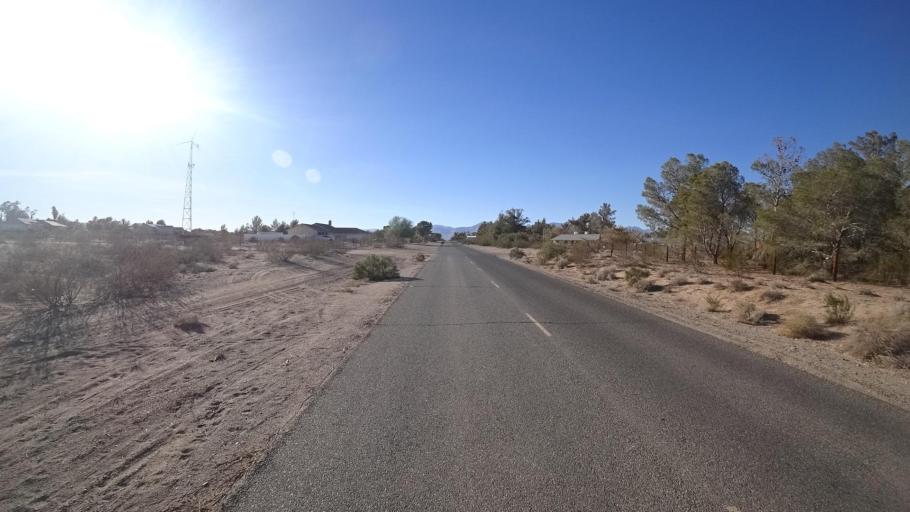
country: US
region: California
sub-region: Kern County
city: Ridgecrest
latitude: 35.6371
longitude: -117.7006
